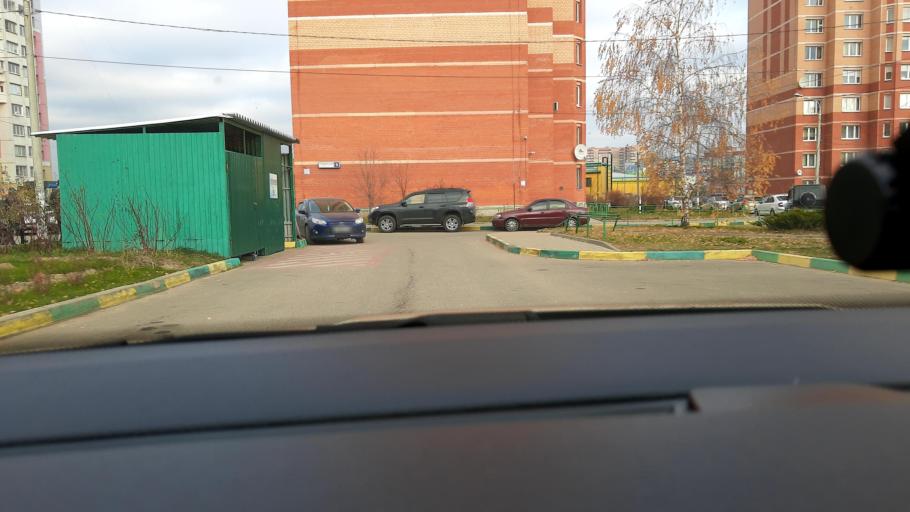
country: RU
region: Moskovskaya
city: Lyubertsy
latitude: 55.6656
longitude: 37.8661
